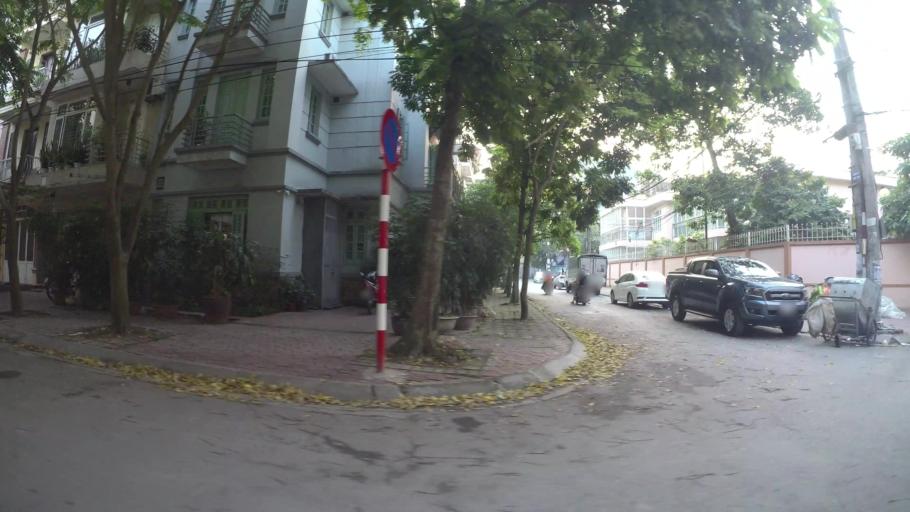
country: VN
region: Ha Noi
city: Cau Giay
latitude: 21.0490
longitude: 105.7956
